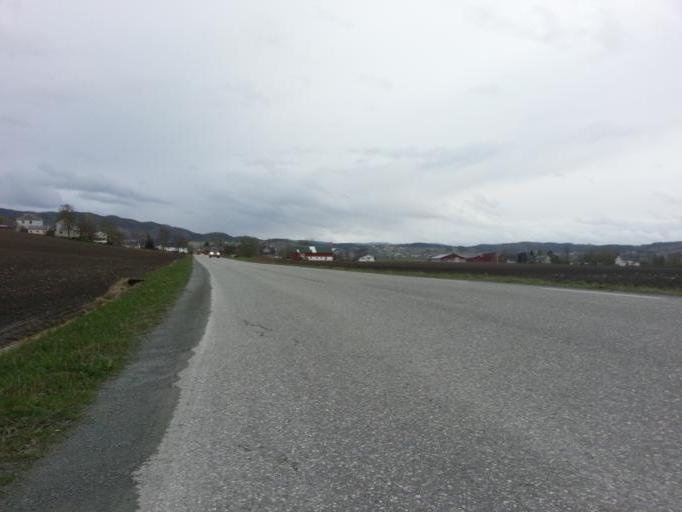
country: NO
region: Nord-Trondelag
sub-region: Levanger
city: Skogn
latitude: 63.6985
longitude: 11.1953
